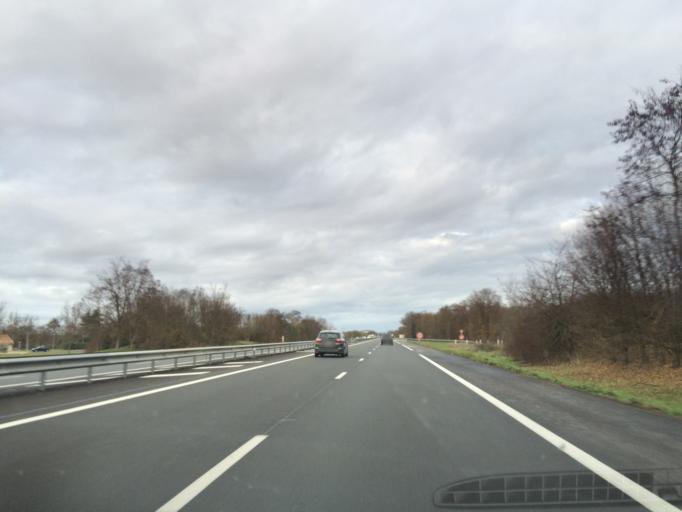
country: FR
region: Poitou-Charentes
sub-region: Departement des Deux-Sevres
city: Fors
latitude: 46.2220
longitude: -0.4488
